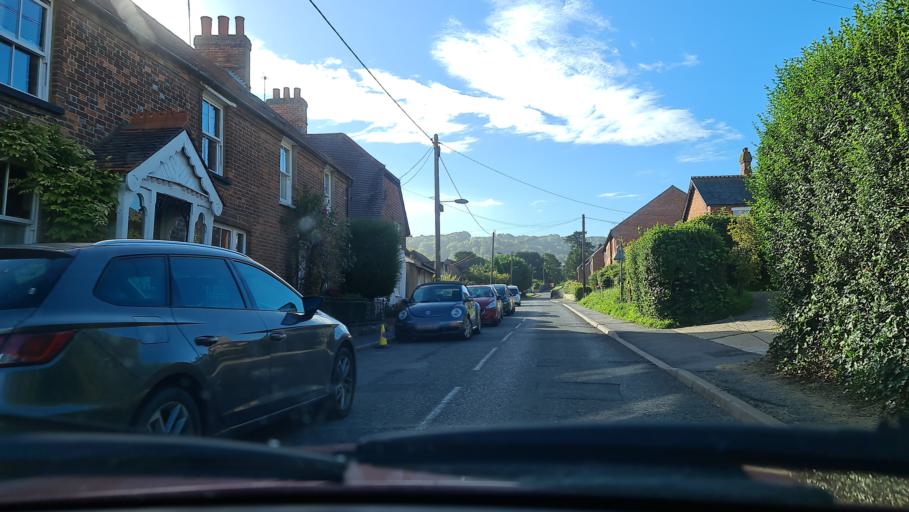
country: GB
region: England
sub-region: Oxfordshire
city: Chinnor
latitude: 51.7005
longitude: -0.9078
